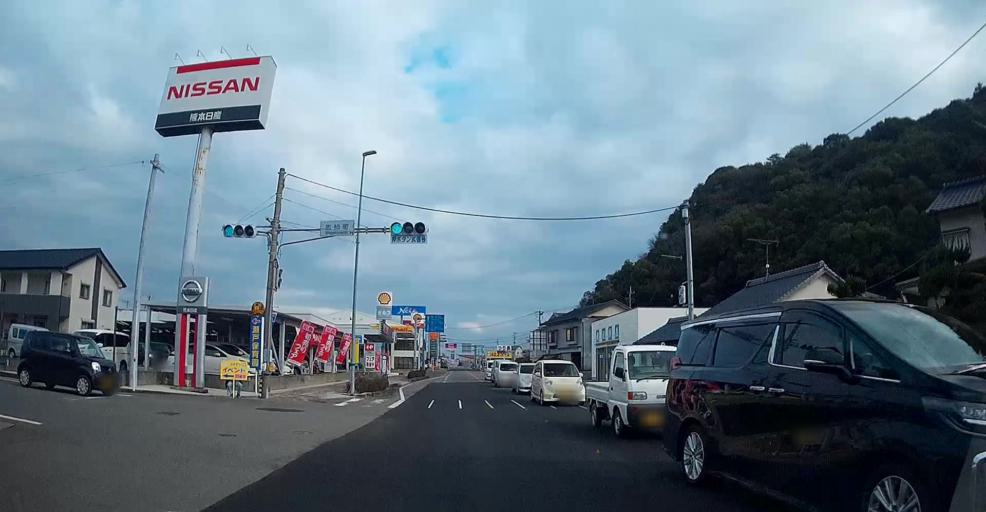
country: JP
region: Kumamoto
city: Hondo
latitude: 32.4492
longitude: 130.2063
